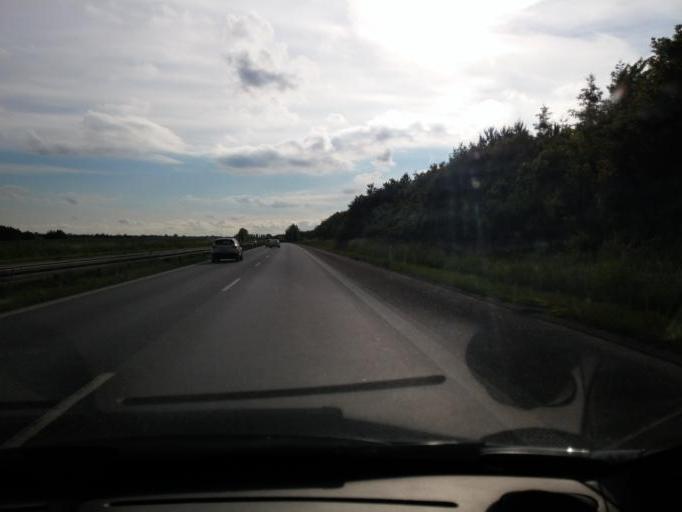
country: DK
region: Zealand
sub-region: Soro Kommune
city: Soro
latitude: 55.4331
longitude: 11.4625
